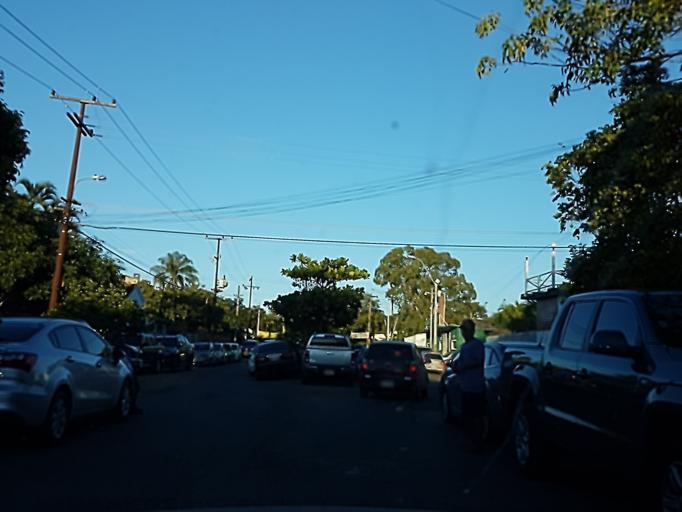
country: PY
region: Asuncion
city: Asuncion
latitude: -25.2569
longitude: -57.5764
